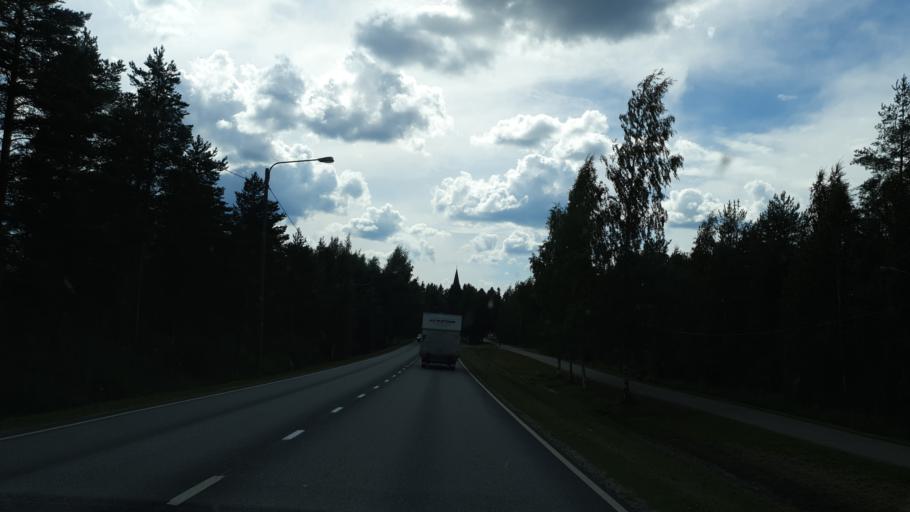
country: FI
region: Kainuu
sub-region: Kajaani
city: Sotkamo
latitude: 64.1362
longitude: 28.4106
